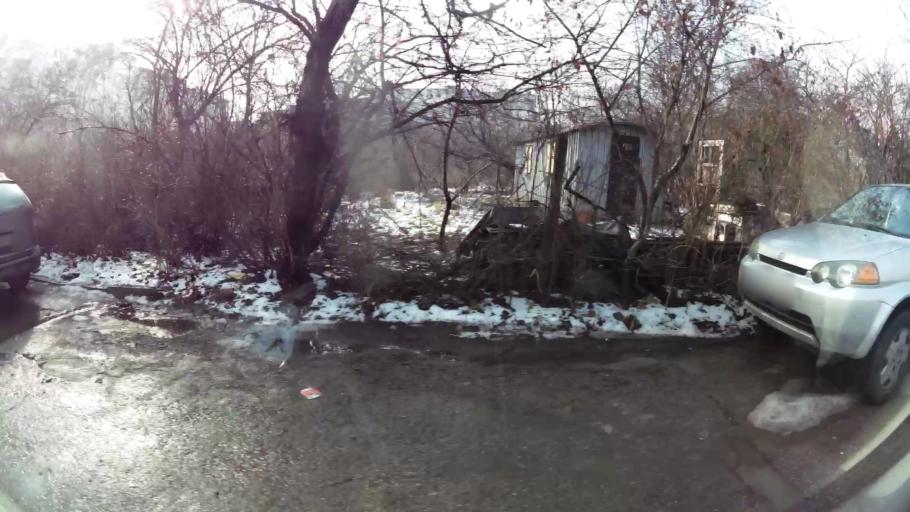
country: BG
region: Sofia-Capital
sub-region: Stolichna Obshtina
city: Sofia
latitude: 42.7179
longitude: 23.2675
